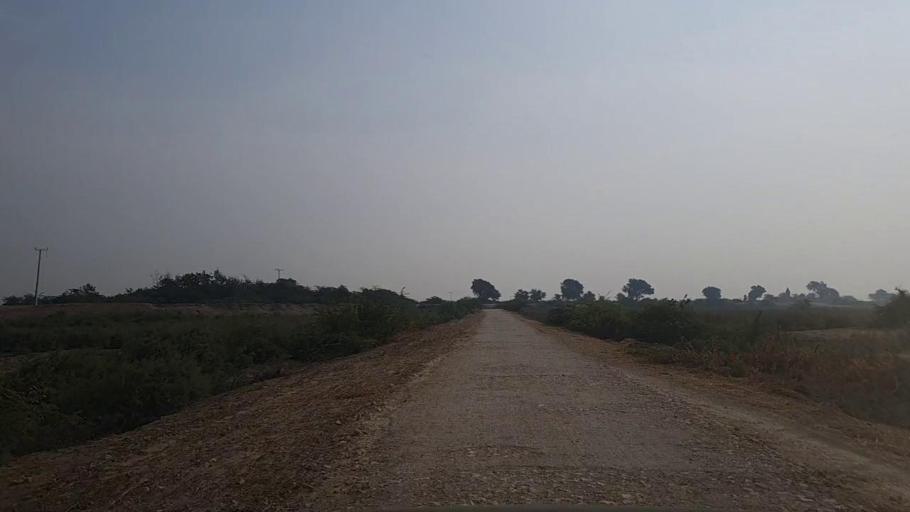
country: PK
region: Sindh
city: Mirpur Sakro
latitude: 24.3774
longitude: 67.7554
